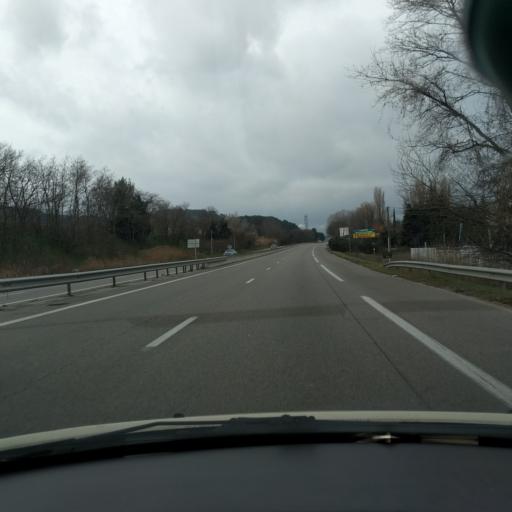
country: FR
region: Provence-Alpes-Cote d'Azur
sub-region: Departement des Bouches-du-Rhone
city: Simiane-Collongue
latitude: 43.4331
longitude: 5.4207
